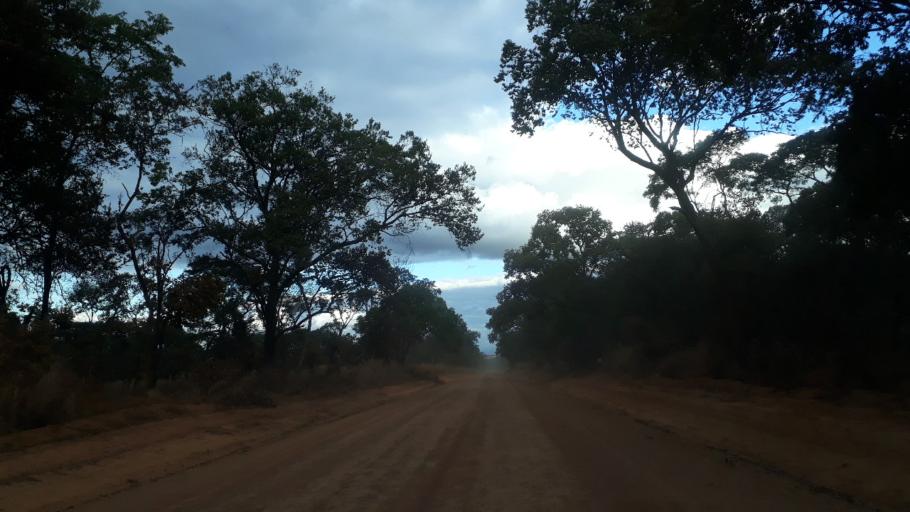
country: ZM
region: Copperbelt
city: Mufulira
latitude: -12.3523
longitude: 28.1006
